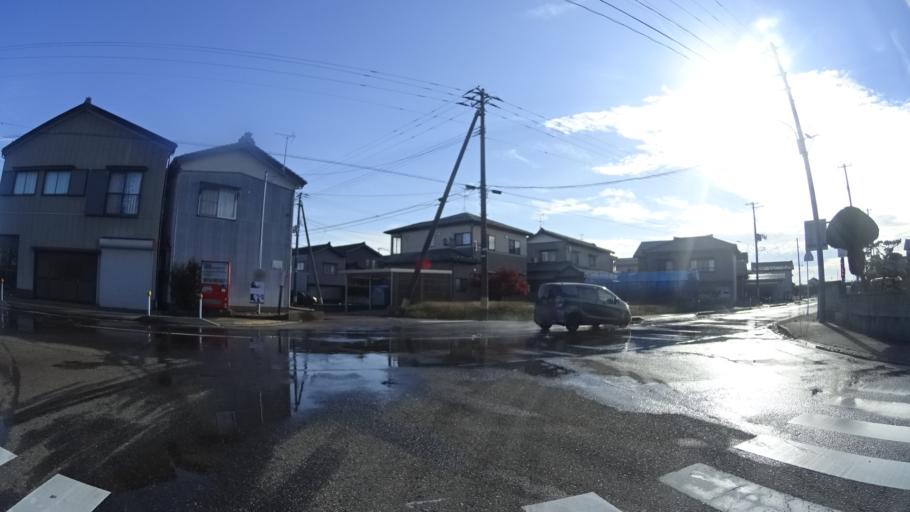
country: JP
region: Niigata
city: Yoshida-kasugacho
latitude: 37.6292
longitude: 138.8358
